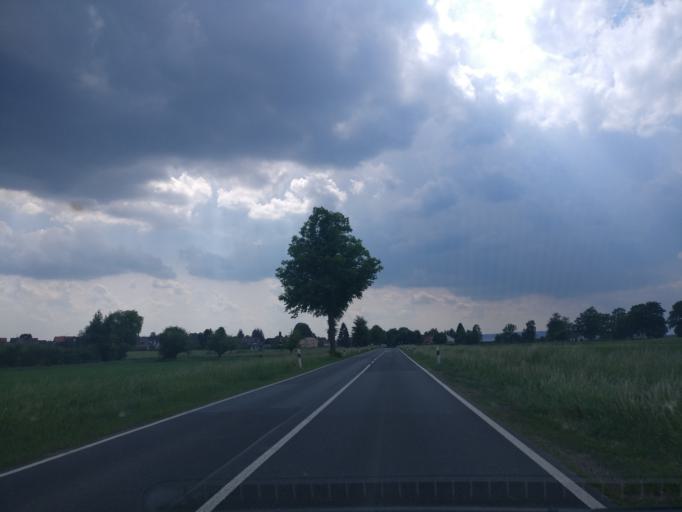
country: DE
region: Hesse
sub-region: Regierungsbezirk Kassel
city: Fuldatal
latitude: 51.3586
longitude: 9.5981
